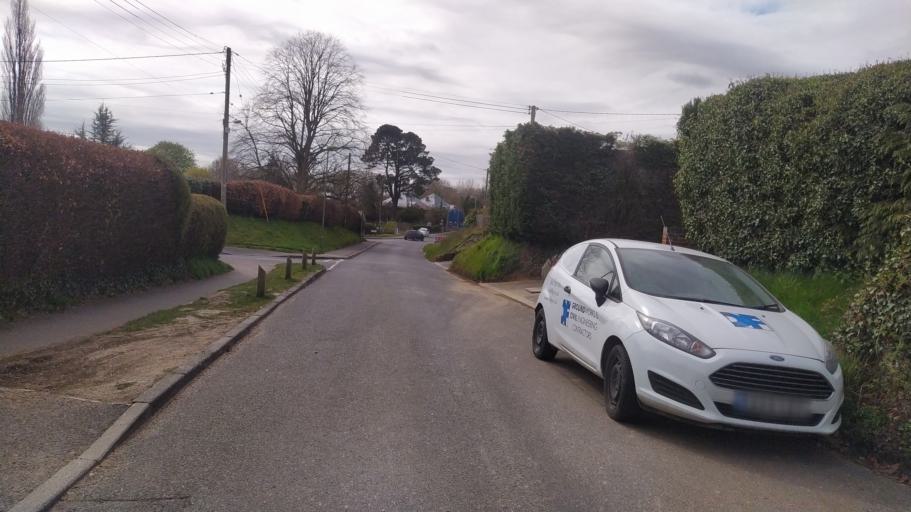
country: GB
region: England
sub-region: Hampshire
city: Bishops Waltham
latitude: 50.9527
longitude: -1.2086
